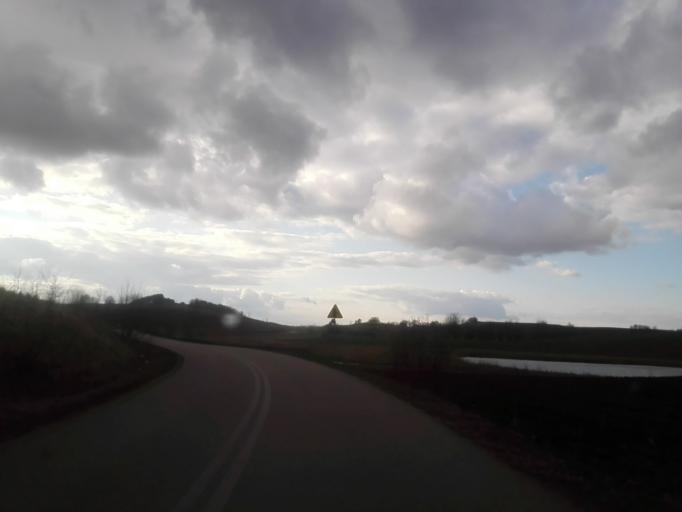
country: PL
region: Podlasie
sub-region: Suwalki
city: Suwalki
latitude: 54.2001
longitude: 22.9924
